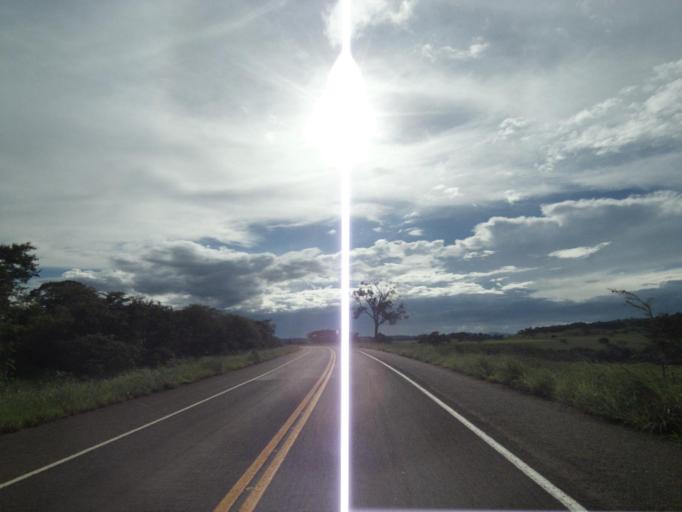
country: BR
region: Goias
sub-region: Jaragua
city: Jaragua
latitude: -15.8919
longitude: -49.5139
